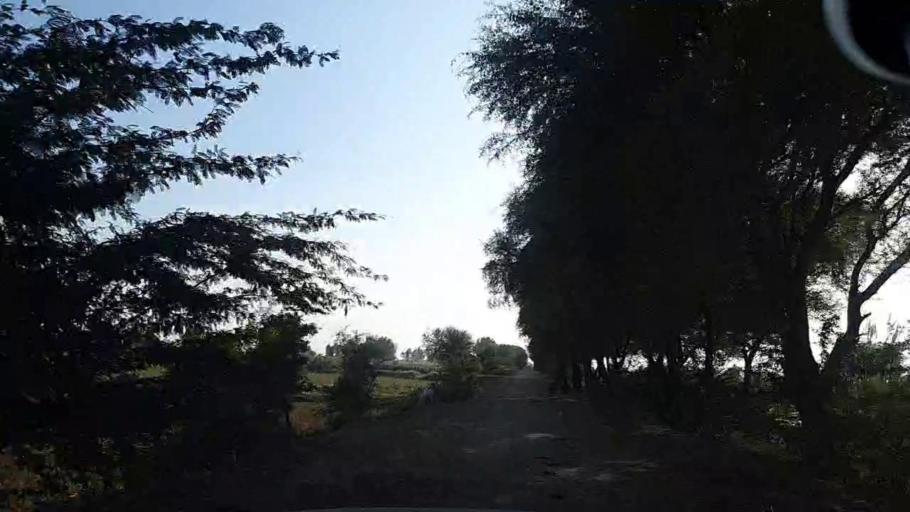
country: PK
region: Sindh
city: Chuhar Jamali
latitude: 24.5647
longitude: 68.0409
